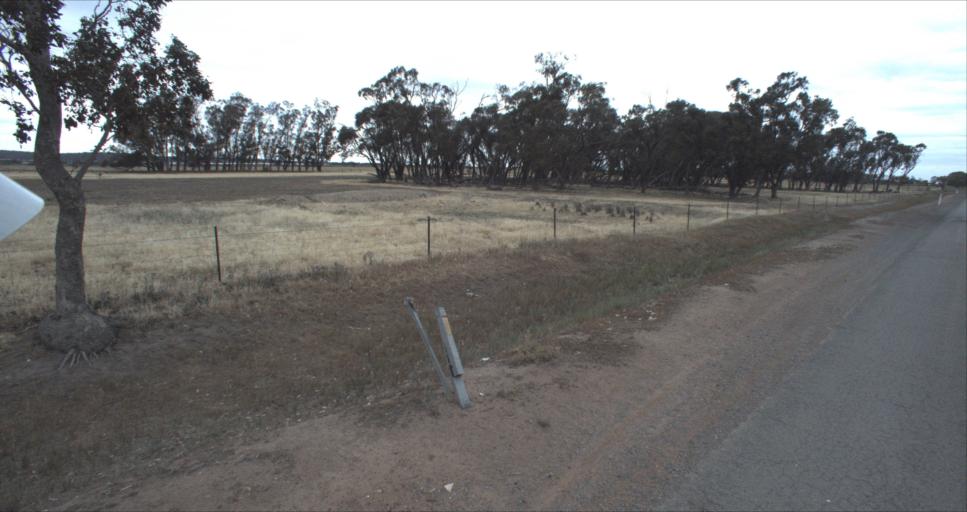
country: AU
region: New South Wales
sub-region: Leeton
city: Leeton
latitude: -34.4081
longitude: 146.3409
